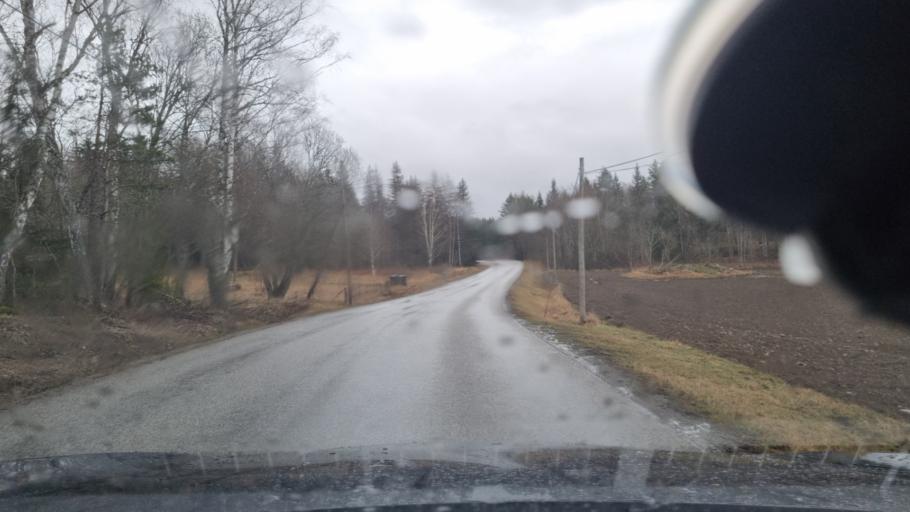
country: SE
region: Stockholm
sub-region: Sigtuna Kommun
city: Sigtuna
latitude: 59.5639
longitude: 17.7057
